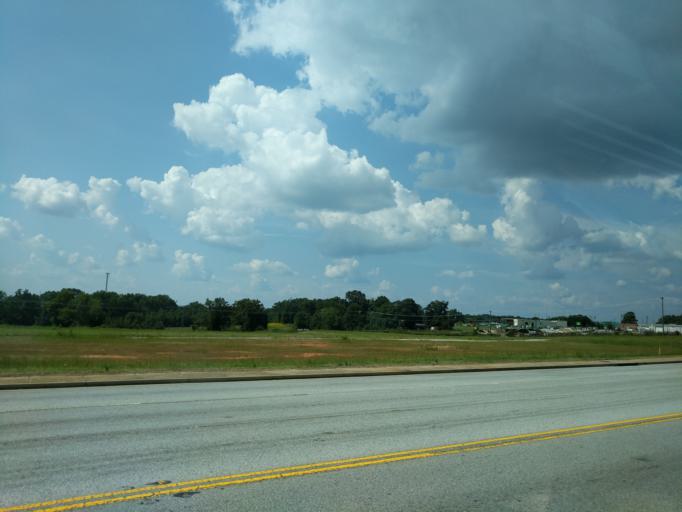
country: US
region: South Carolina
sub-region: Greenville County
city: Five Forks
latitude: 34.8641
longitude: -82.2210
